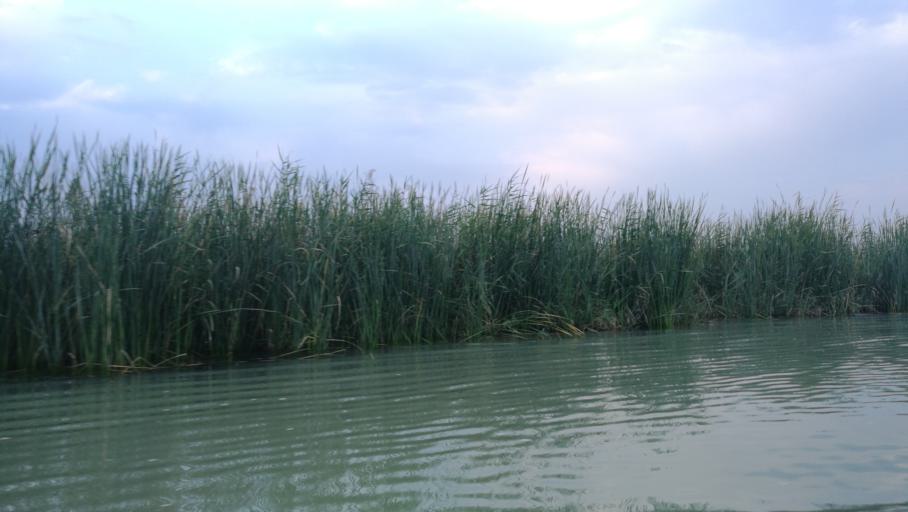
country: IQ
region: Dhi Qar
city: Al Jabayish
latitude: 30.9818
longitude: 47.0423
